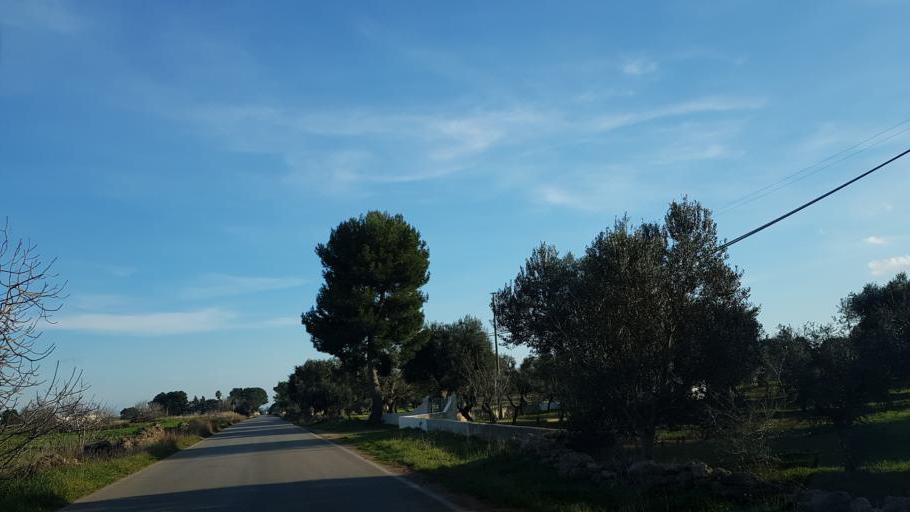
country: IT
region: Apulia
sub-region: Provincia di Brindisi
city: San Vito dei Normanni
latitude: 40.6846
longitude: 17.7666
